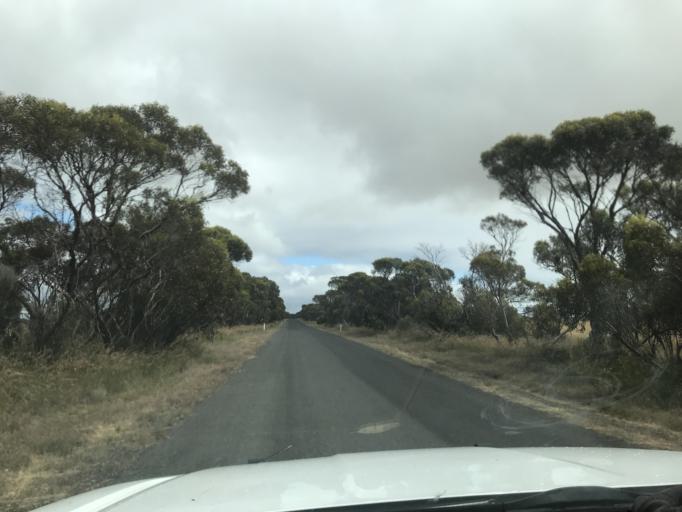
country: AU
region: South Australia
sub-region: Tatiara
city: Bordertown
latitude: -36.1339
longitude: 141.1723
